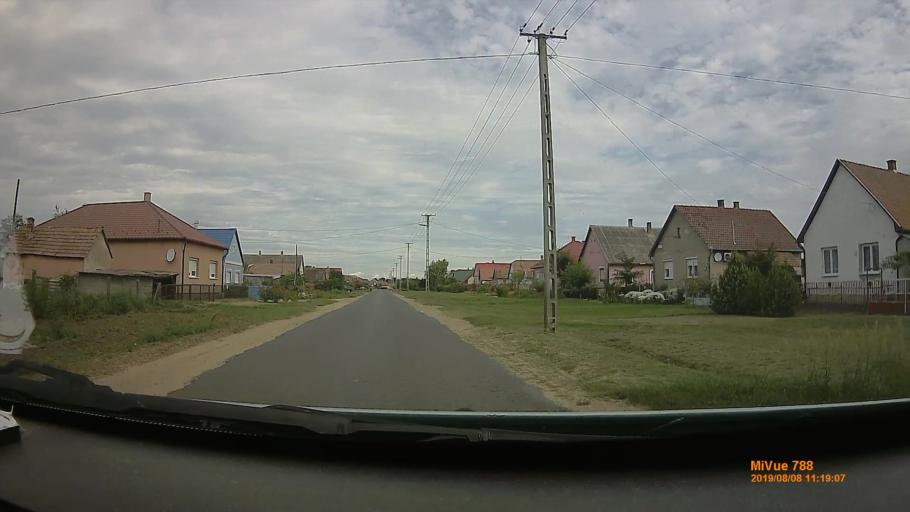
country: HU
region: Szabolcs-Szatmar-Bereg
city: Balkany
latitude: 47.7429
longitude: 21.8390
